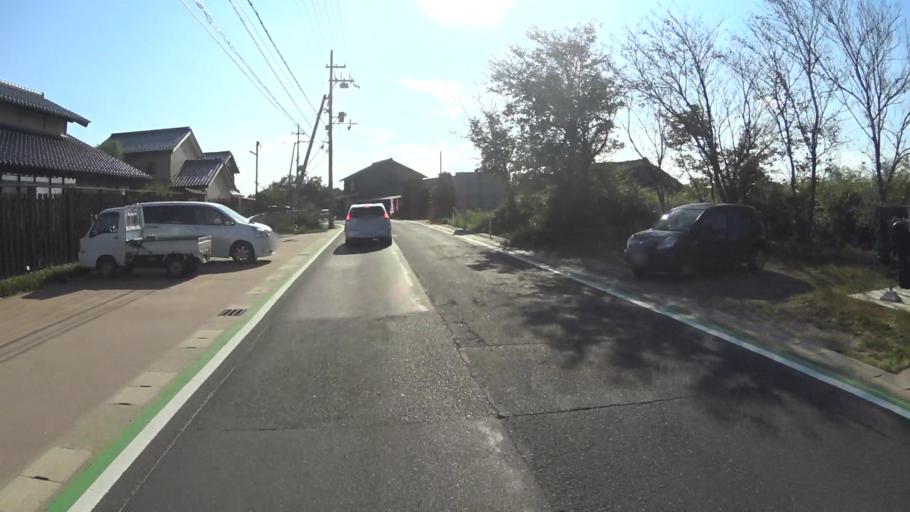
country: JP
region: Hyogo
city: Toyooka
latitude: 35.6547
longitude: 134.9542
